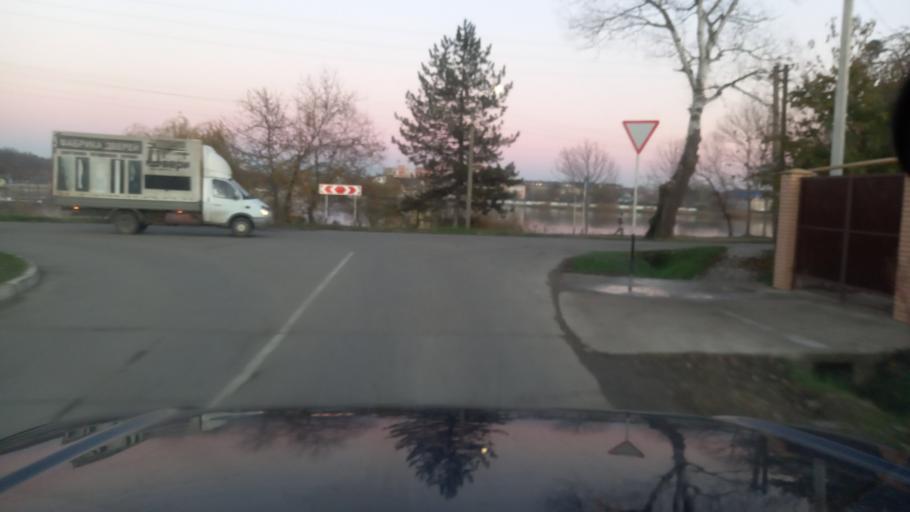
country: RU
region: Krasnodarskiy
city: Goryachiy Klyuch
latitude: 44.6335
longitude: 39.1177
